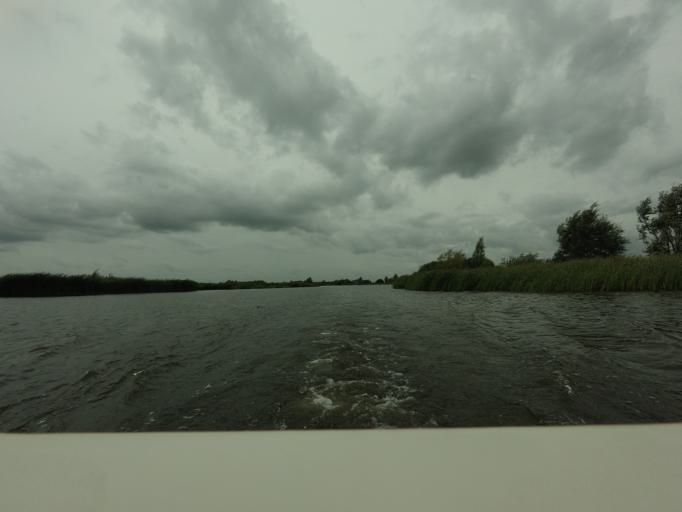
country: NL
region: Friesland
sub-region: Gemeente Boarnsterhim
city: Aldeboarn
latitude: 53.0991
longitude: 5.9176
